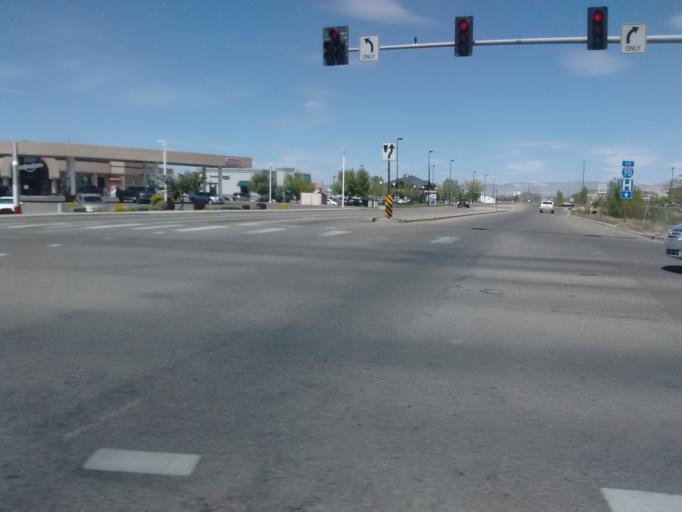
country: US
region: Colorado
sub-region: Mesa County
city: Redlands
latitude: 39.0946
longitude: -108.6080
